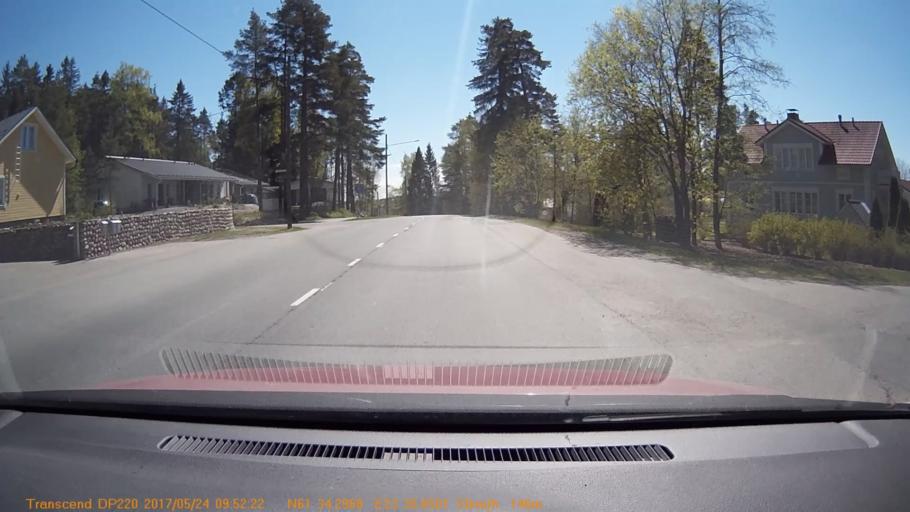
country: FI
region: Pirkanmaa
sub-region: Tampere
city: Yloejaervi
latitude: 61.5716
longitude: 23.5941
